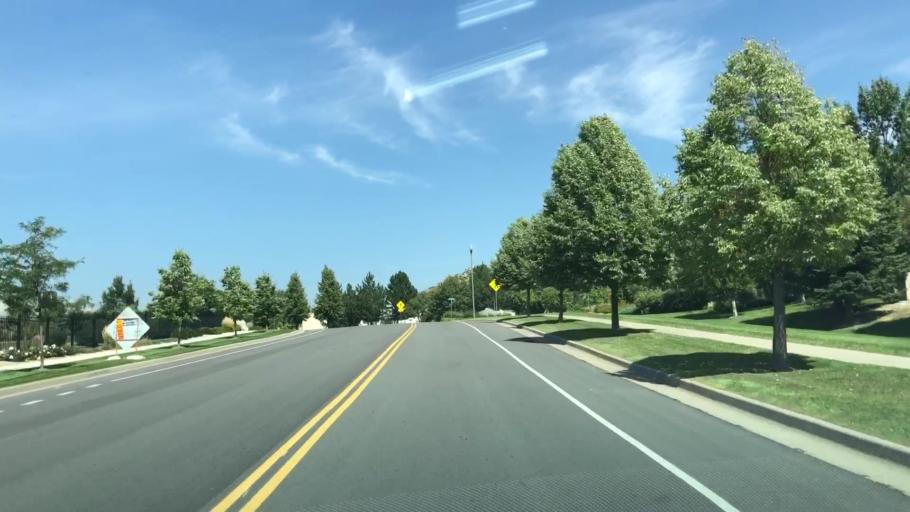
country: US
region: Colorado
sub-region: Larimer County
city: Loveland
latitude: 40.3936
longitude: -105.1408
